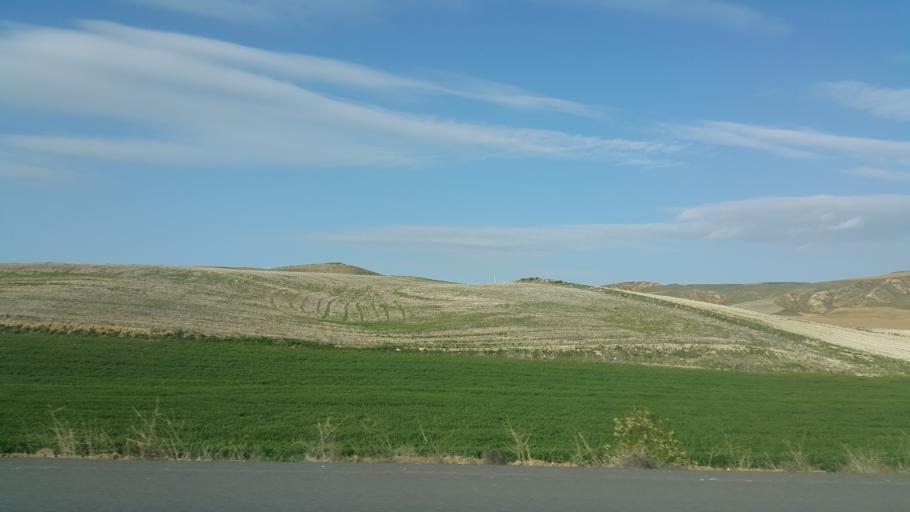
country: TR
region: Ankara
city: Sereflikochisar
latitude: 39.0574
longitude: 33.4299
